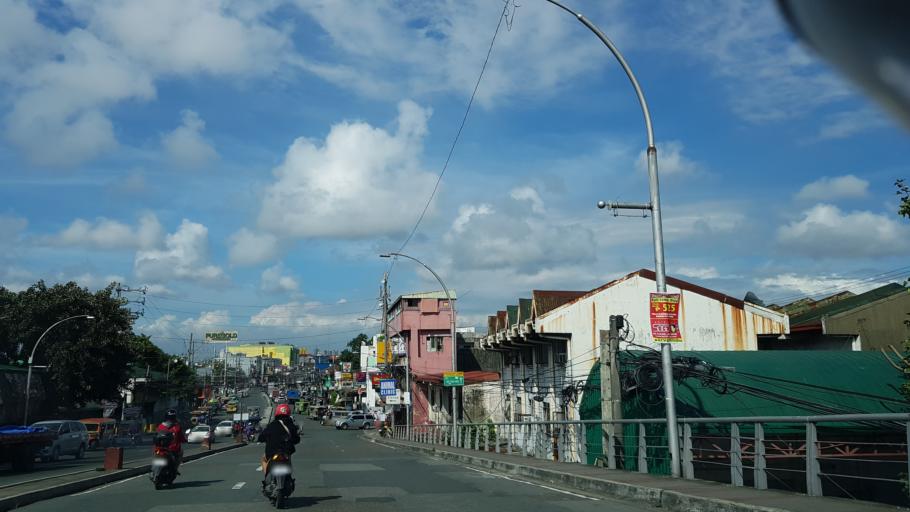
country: PH
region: Metro Manila
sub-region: San Juan
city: San Juan
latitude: 14.5868
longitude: 121.0203
